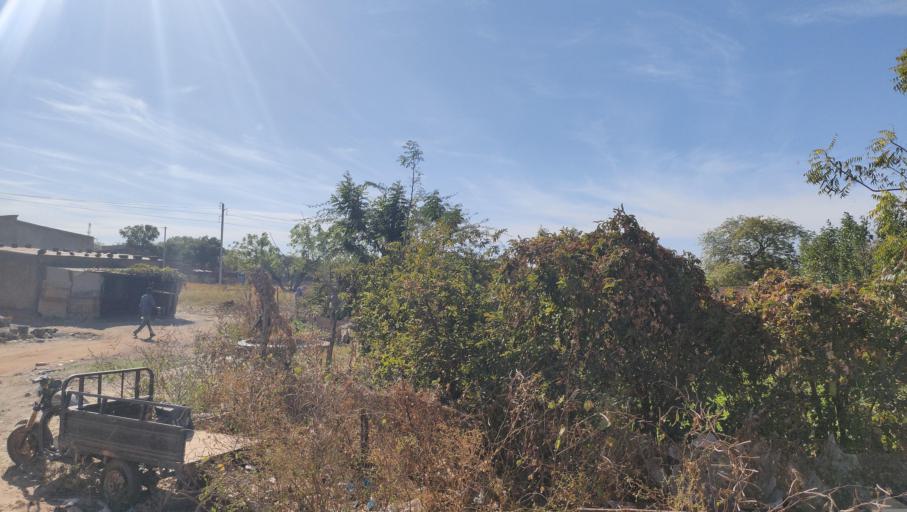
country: BF
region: Est
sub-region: Province du Gourma
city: Fada N'gourma
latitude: 12.0649
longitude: 0.3633
